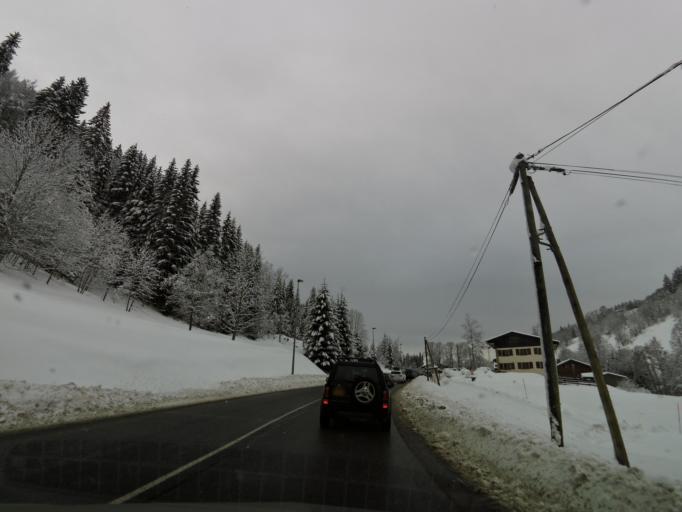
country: FR
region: Rhone-Alpes
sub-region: Departement de la Haute-Savoie
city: Les Gets
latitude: 46.1664
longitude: 6.6763
